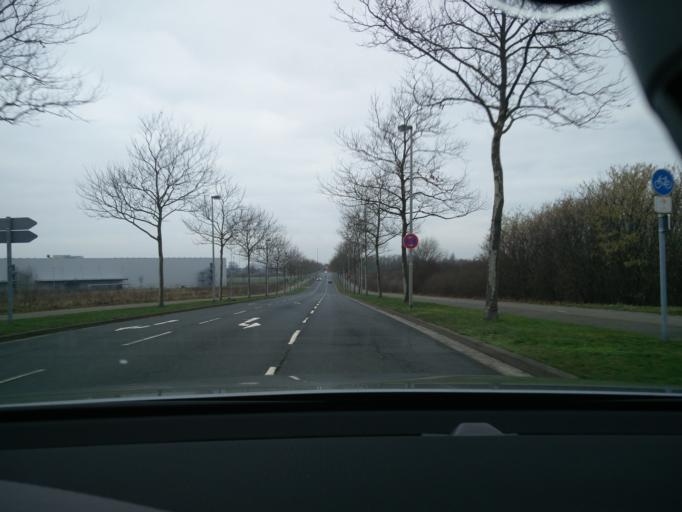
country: DE
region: Lower Saxony
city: Laatzen
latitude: 52.3301
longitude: 9.8263
